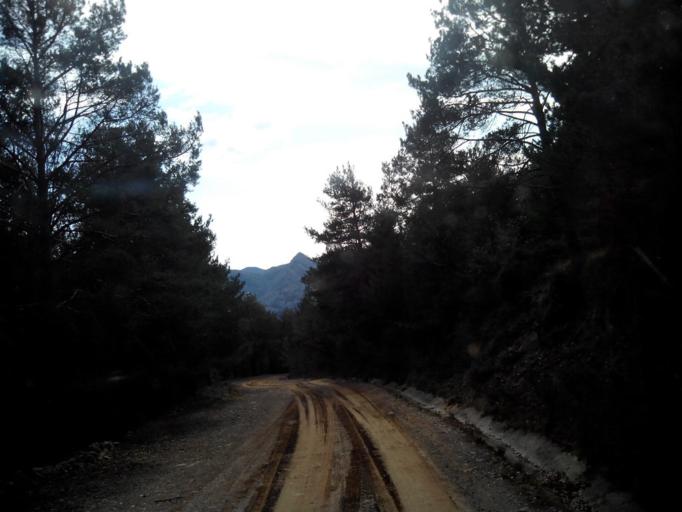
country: ES
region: Catalonia
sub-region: Provincia de Barcelona
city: Vilada
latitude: 42.1572
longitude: 1.9294
